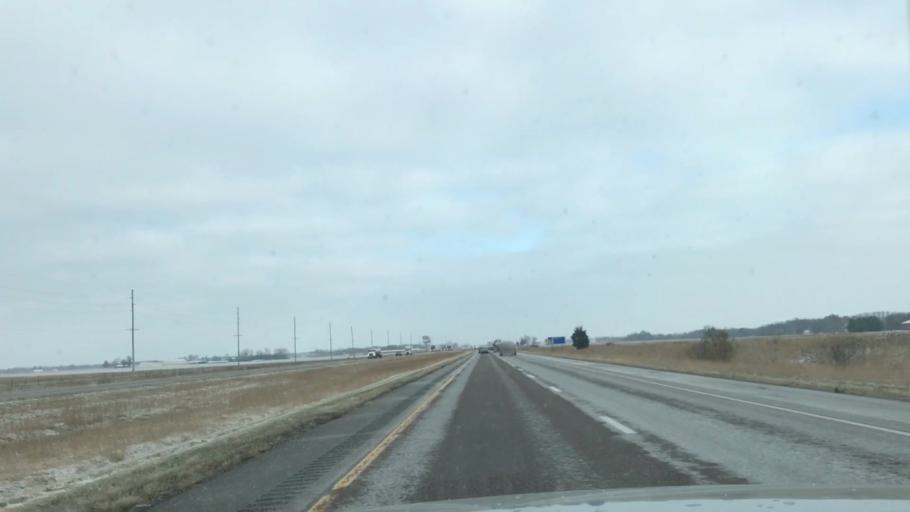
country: US
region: Illinois
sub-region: Macoupin County
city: Staunton
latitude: 38.9942
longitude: -89.7496
